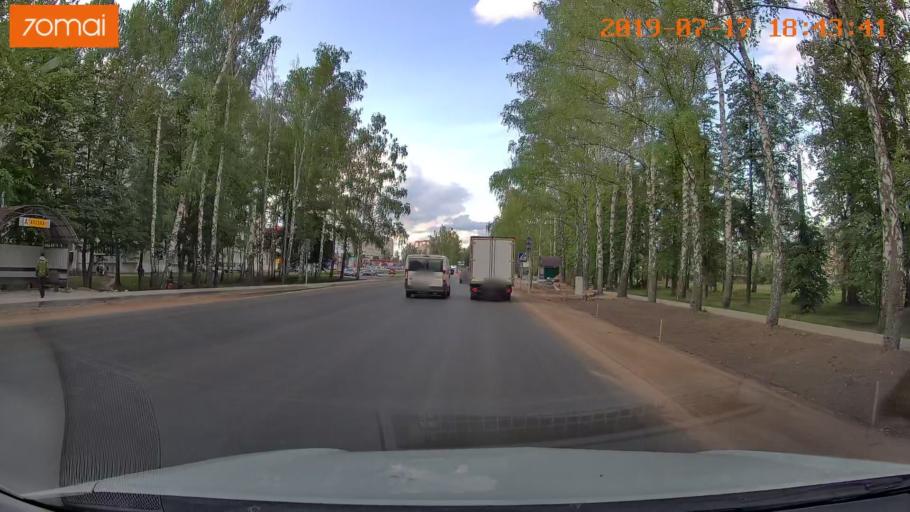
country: BY
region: Mogilev
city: Asipovichy
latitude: 53.3162
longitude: 28.6442
